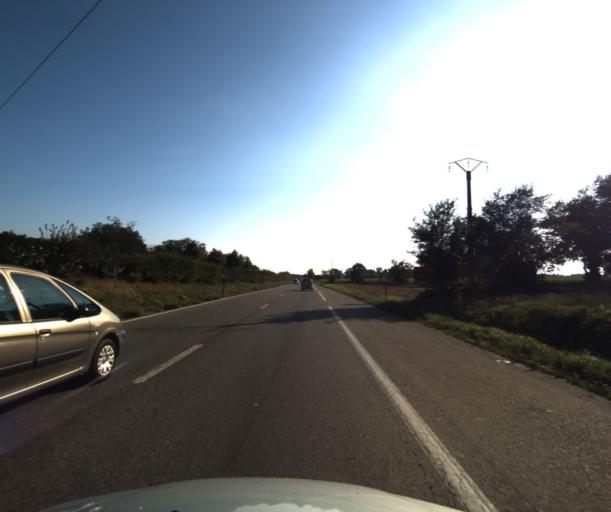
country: FR
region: Midi-Pyrenees
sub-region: Departement de la Haute-Garonne
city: Saubens
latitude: 43.4965
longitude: 1.3478
